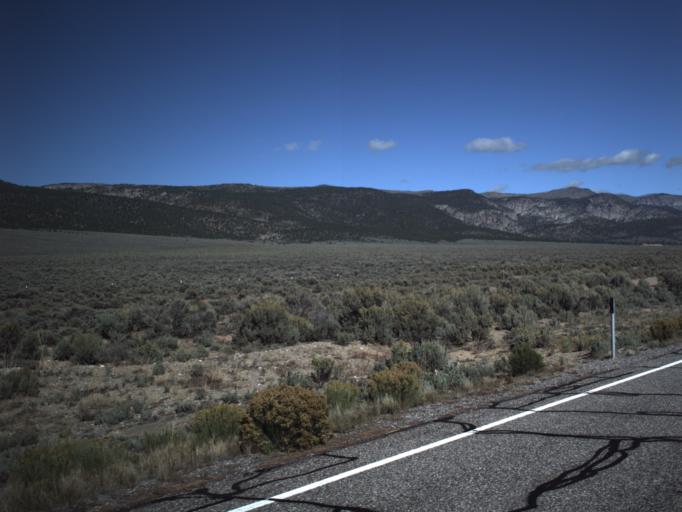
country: US
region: Utah
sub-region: Piute County
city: Junction
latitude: 38.2564
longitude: -111.9862
